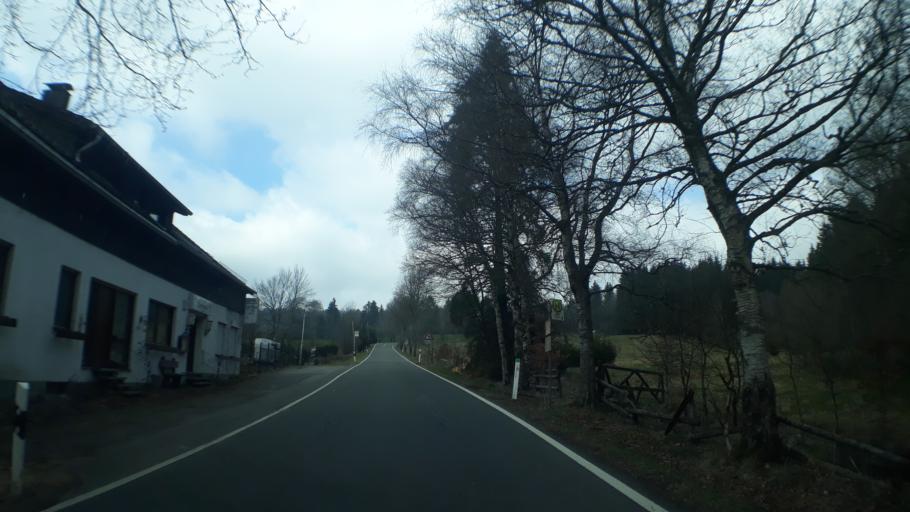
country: DE
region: North Rhine-Westphalia
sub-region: Regierungsbezirk Koln
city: Monschau
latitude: 50.5427
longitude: 6.1938
